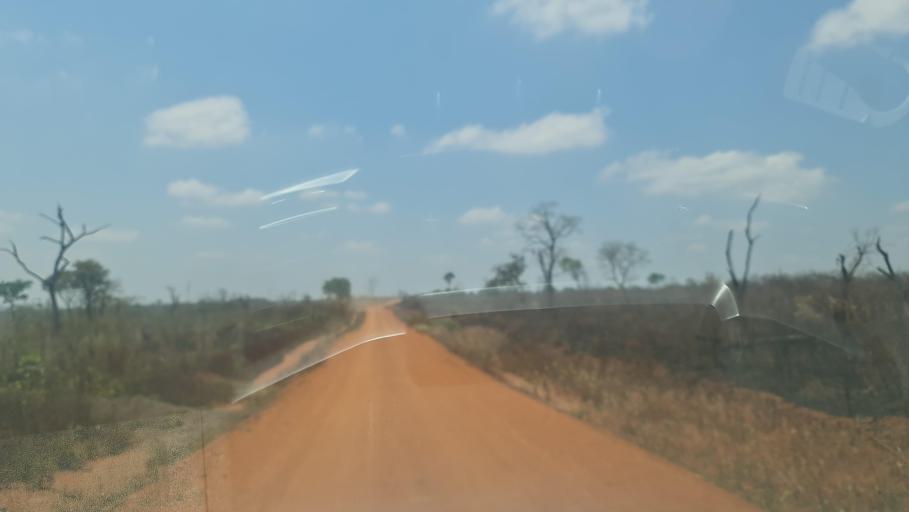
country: MW
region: Southern Region
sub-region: Nsanje District
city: Nsanje
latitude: -17.3393
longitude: 35.7246
